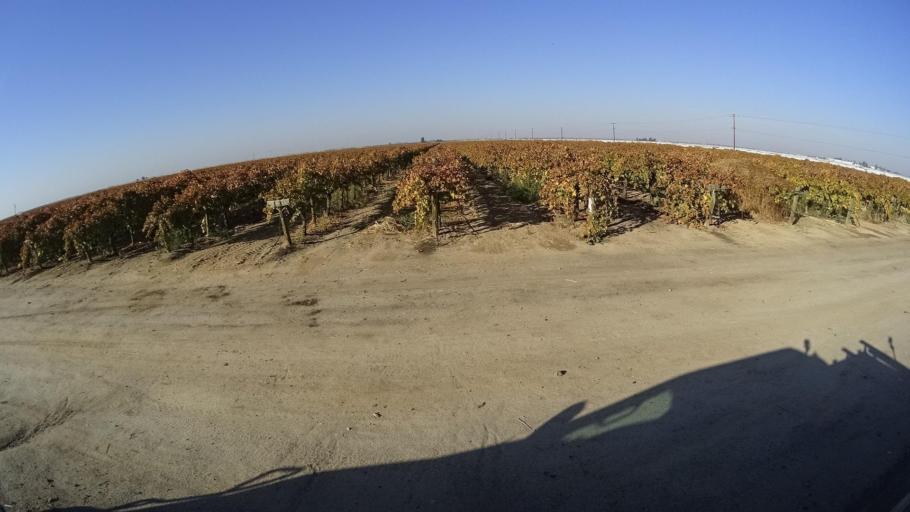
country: US
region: California
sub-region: Tulare County
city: Richgrove
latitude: 35.7609
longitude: -119.1696
